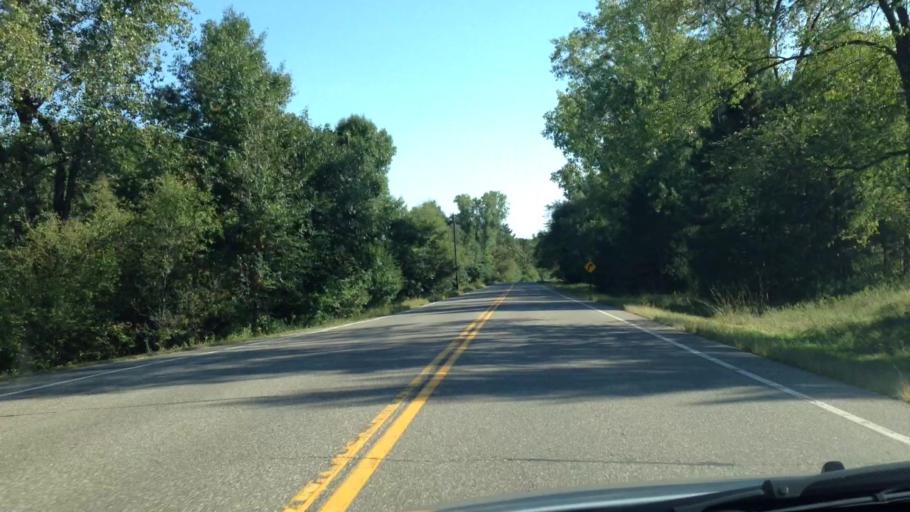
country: US
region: Minnesota
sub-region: Washington County
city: Stillwater
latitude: 45.1195
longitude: -92.8142
